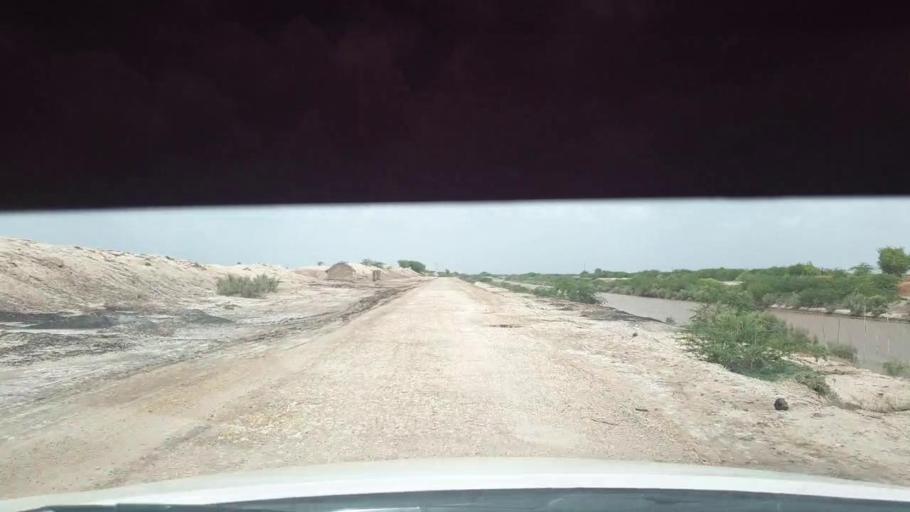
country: PK
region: Sindh
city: Kadhan
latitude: 24.5169
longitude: 69.1208
